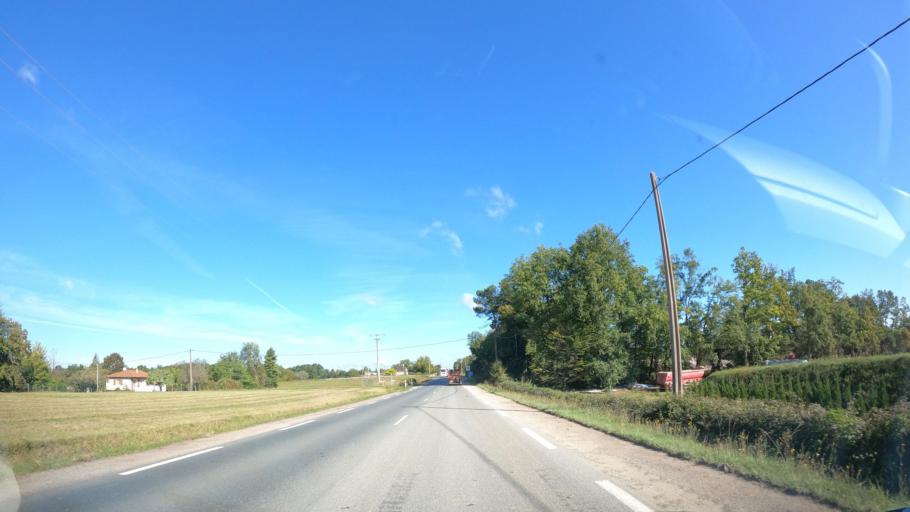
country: FR
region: Aquitaine
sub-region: Departement de la Dordogne
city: Notre-Dame-de-Sanilhac
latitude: 45.1121
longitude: 0.6934
